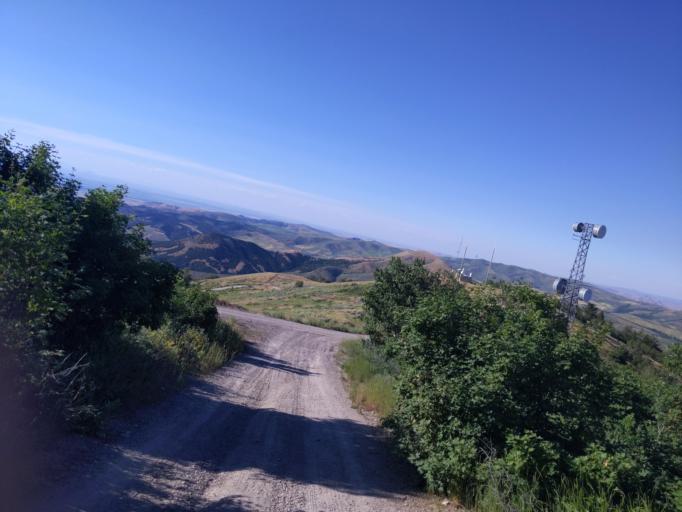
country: US
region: Idaho
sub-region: Bannock County
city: Pocatello
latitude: 42.8491
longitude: -112.3625
